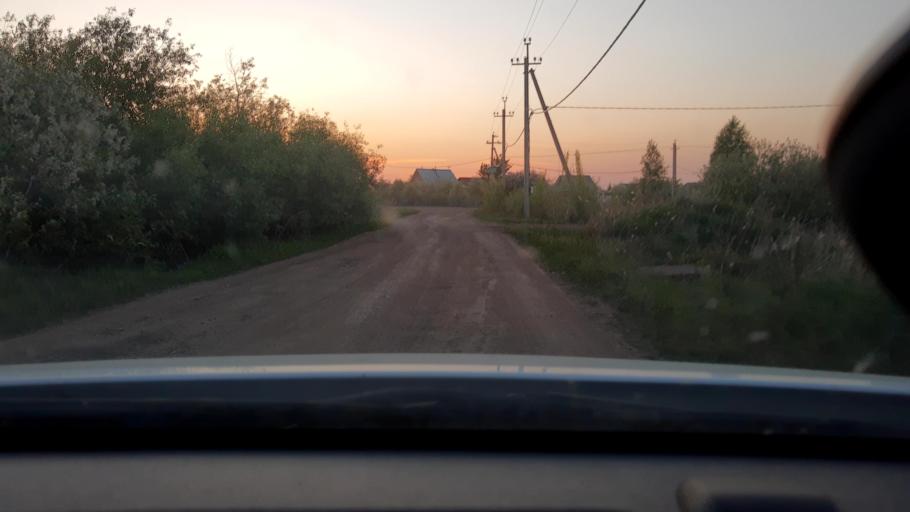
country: RU
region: Bashkortostan
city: Avdon
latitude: 54.5272
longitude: 55.8217
